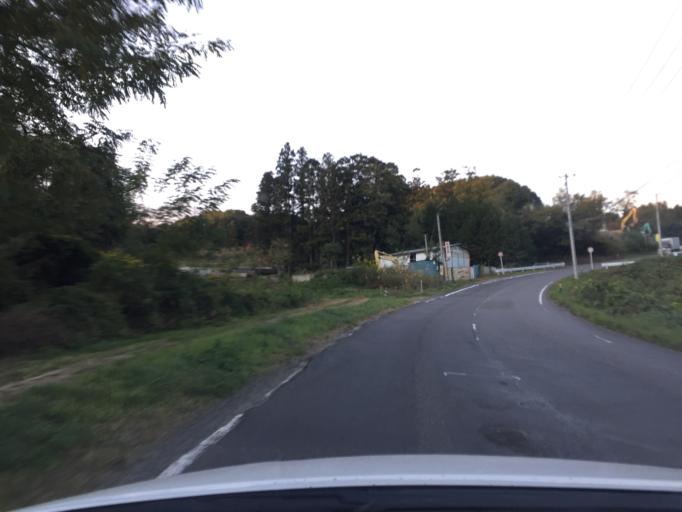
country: JP
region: Fukushima
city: Sukagawa
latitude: 37.3310
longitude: 140.4398
